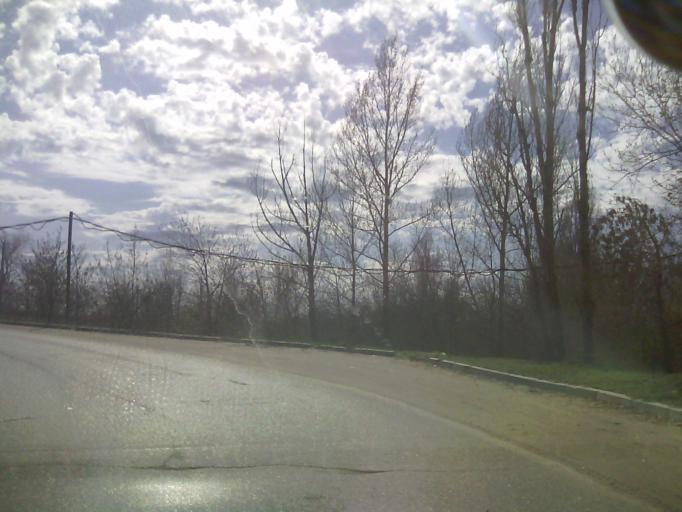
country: RU
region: Saratov
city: Sokolovyy
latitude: 51.5919
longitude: 45.9051
